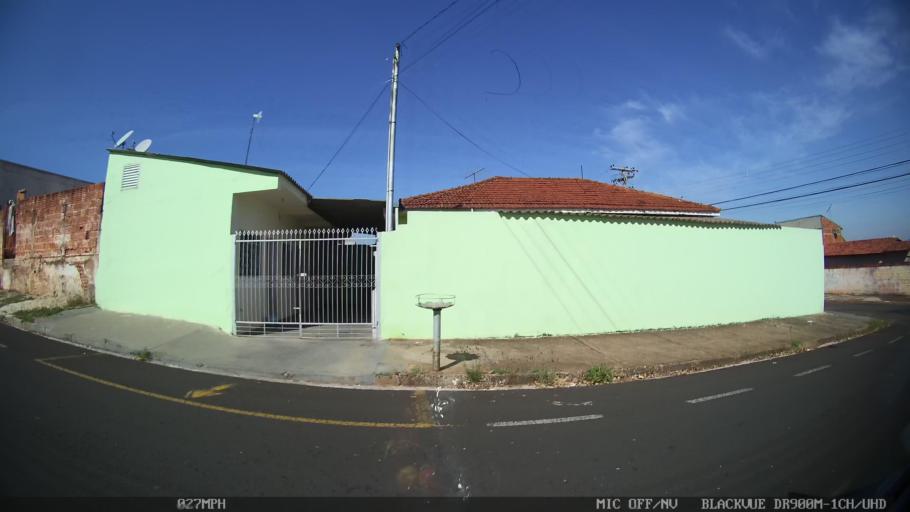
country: BR
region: Sao Paulo
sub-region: Sao Jose Do Rio Preto
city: Sao Jose do Rio Preto
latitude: -20.7856
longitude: -49.4140
